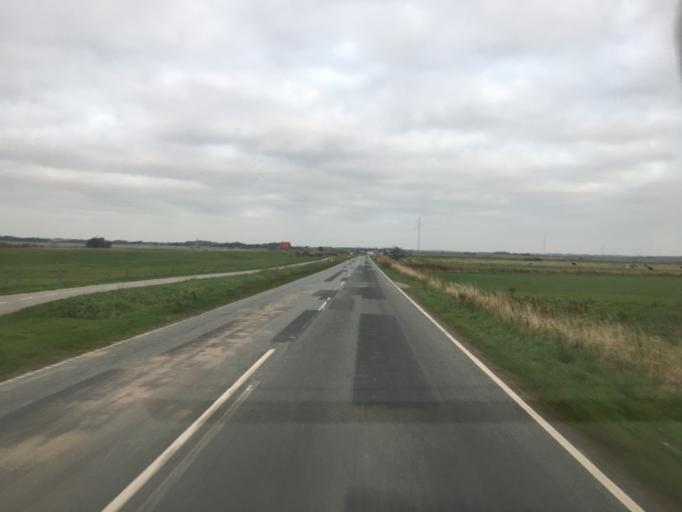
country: DE
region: Schleswig-Holstein
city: Rodenas
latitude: 54.9629
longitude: 8.7091
